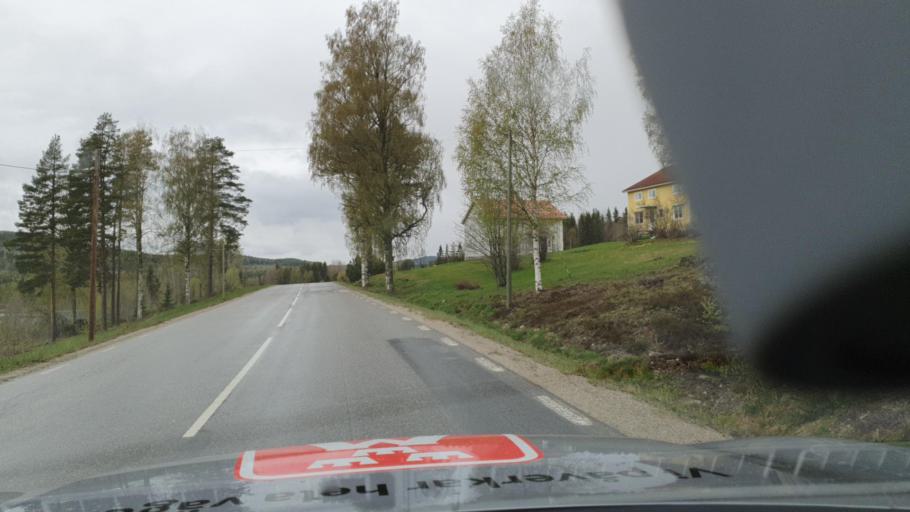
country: SE
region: Vaesternorrland
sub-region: OErnskoeldsviks Kommun
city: Bredbyn
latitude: 63.5153
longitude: 17.7460
